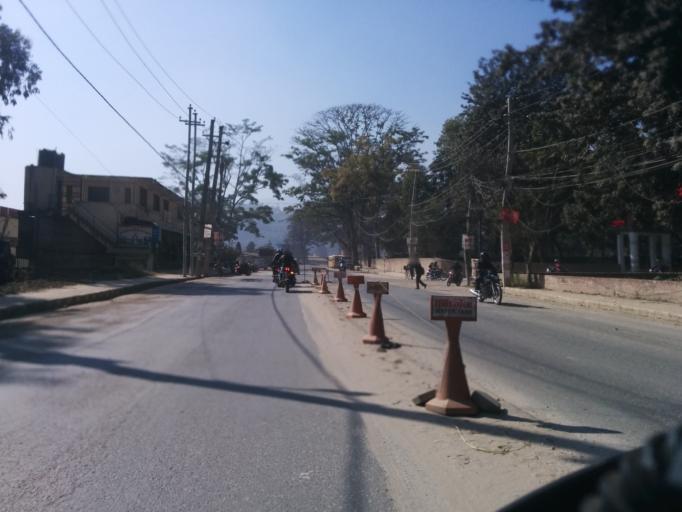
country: NP
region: Central Region
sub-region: Bagmati Zone
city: Patan
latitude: 27.6790
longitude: 85.2973
